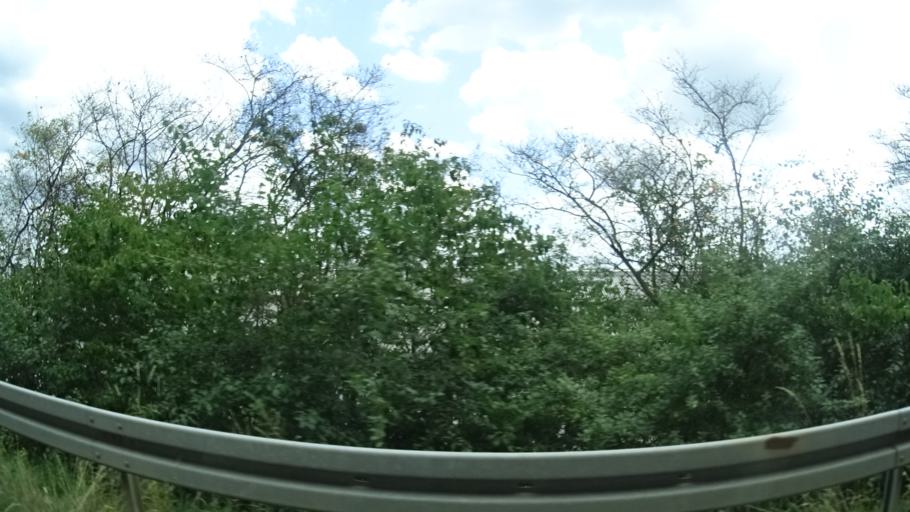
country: DE
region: Hesse
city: Gedern
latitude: 50.4167
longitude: 9.2263
